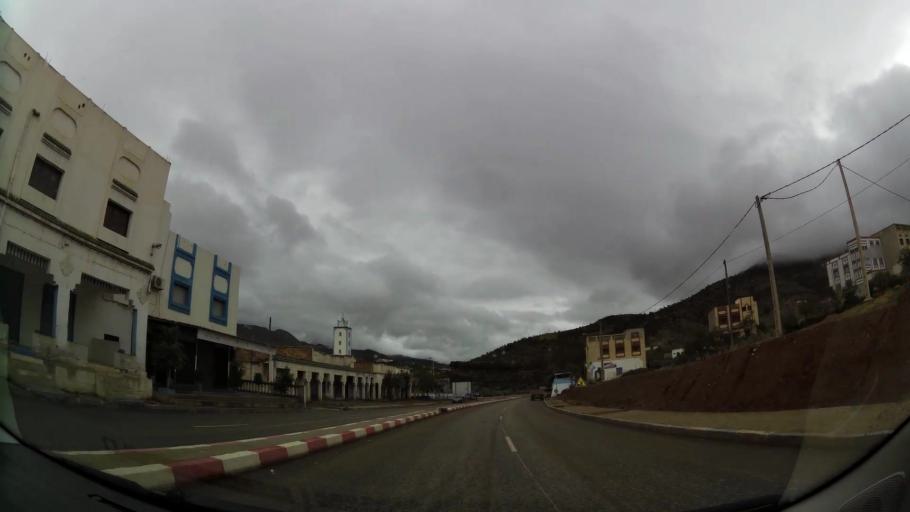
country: MA
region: Taza-Al Hoceima-Taounate
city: Imzourene
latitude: 34.9668
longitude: -3.8138
